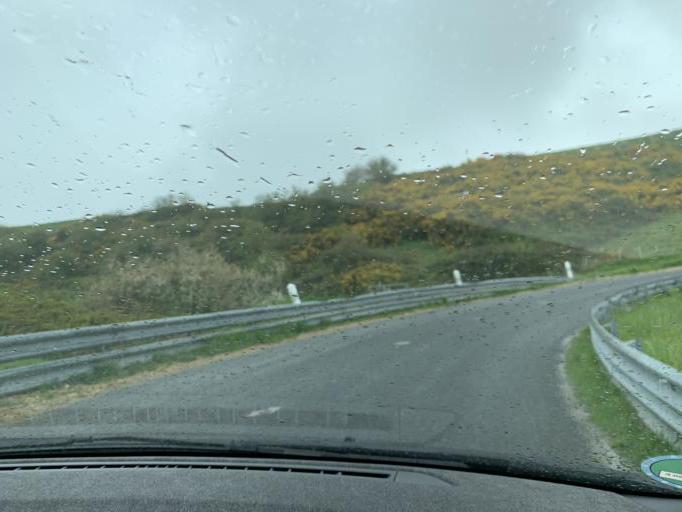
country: FR
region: Haute-Normandie
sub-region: Departement de la Seine-Maritime
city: Etretat
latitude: 49.7130
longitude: 0.2301
